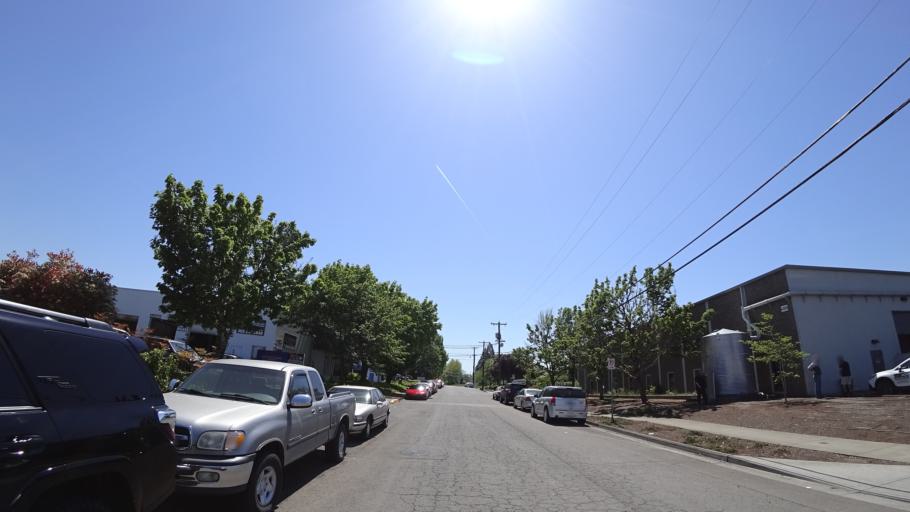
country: US
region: Oregon
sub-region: Washington County
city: Beaverton
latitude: 45.4881
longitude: -122.8224
